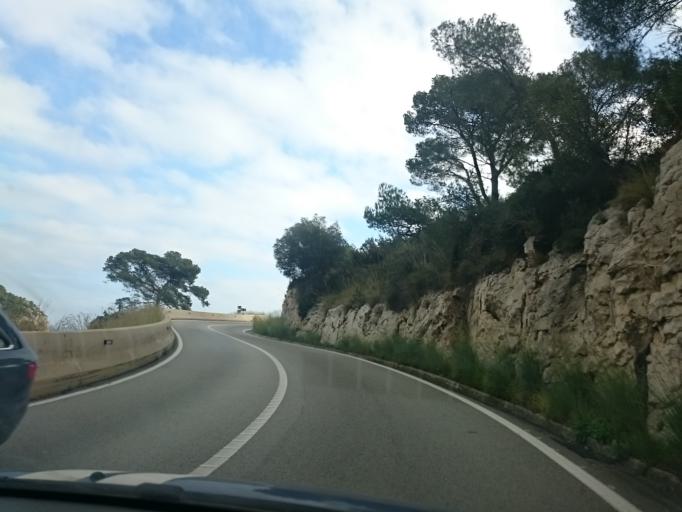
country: ES
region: Catalonia
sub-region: Provincia de Barcelona
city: Sitges
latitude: 41.2501
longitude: 1.8896
